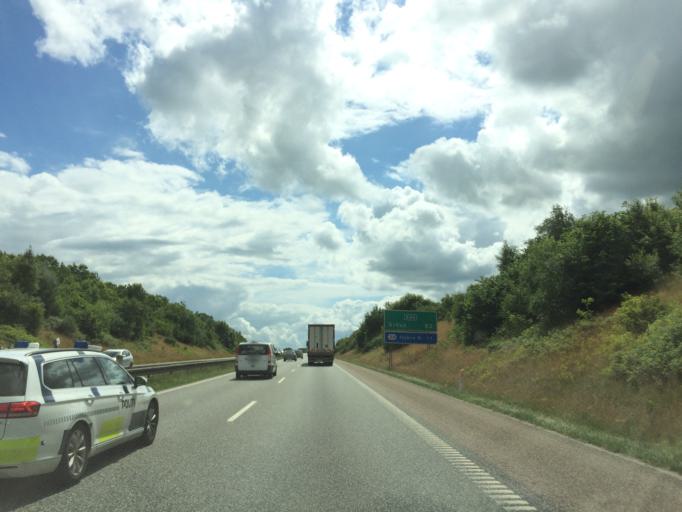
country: DK
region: North Denmark
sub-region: Mariagerfjord Kommune
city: Hobro
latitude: 56.7726
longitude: 9.6940
